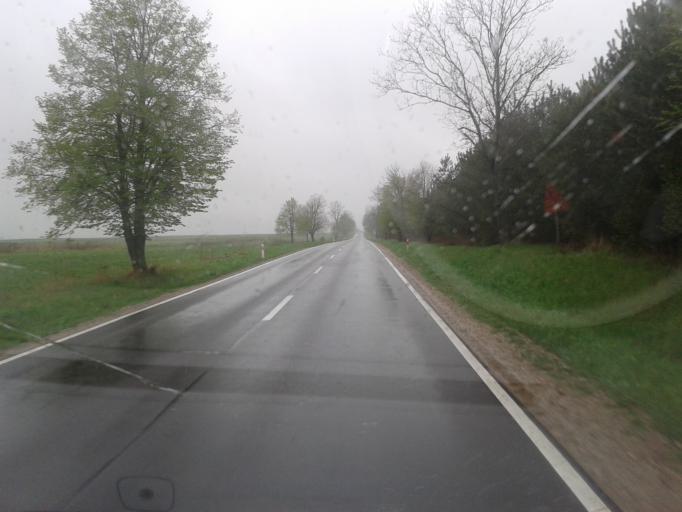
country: PL
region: Subcarpathian Voivodeship
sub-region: Powiat lubaczowski
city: Cieszanow
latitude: 50.2644
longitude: 23.1454
